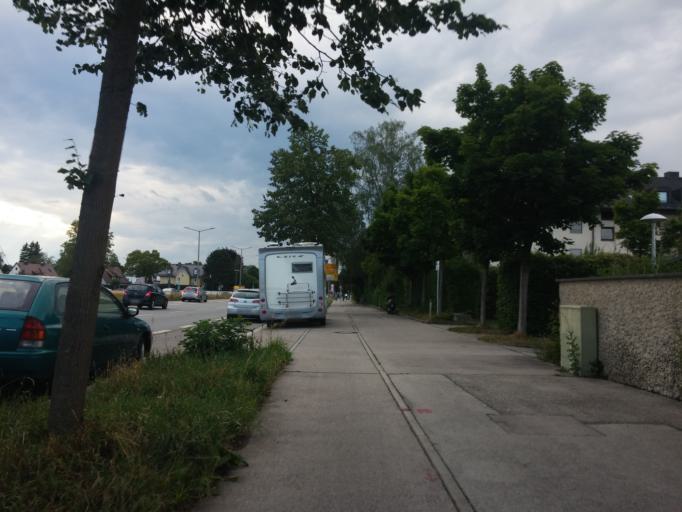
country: DE
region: Bavaria
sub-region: Upper Bavaria
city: Haar
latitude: 48.1058
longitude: 11.7386
